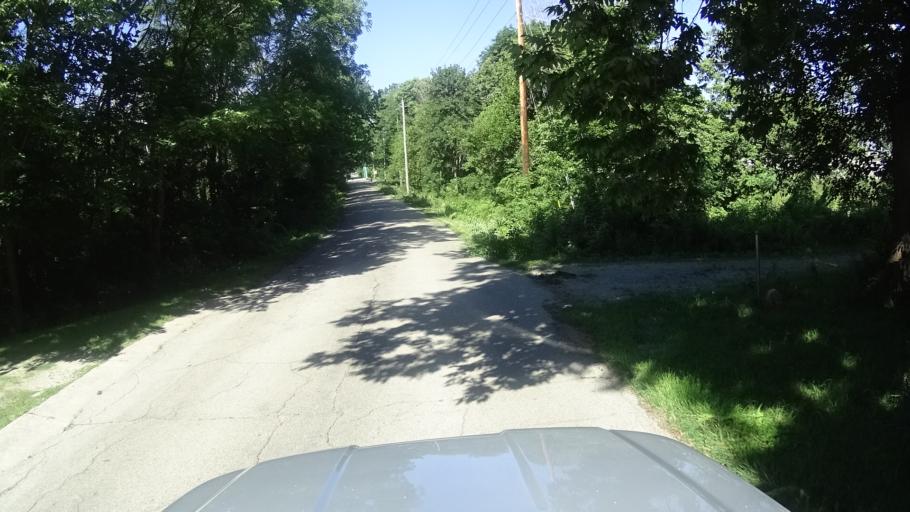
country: US
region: Indiana
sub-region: Madison County
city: Pendleton
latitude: 40.0086
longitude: -85.7330
